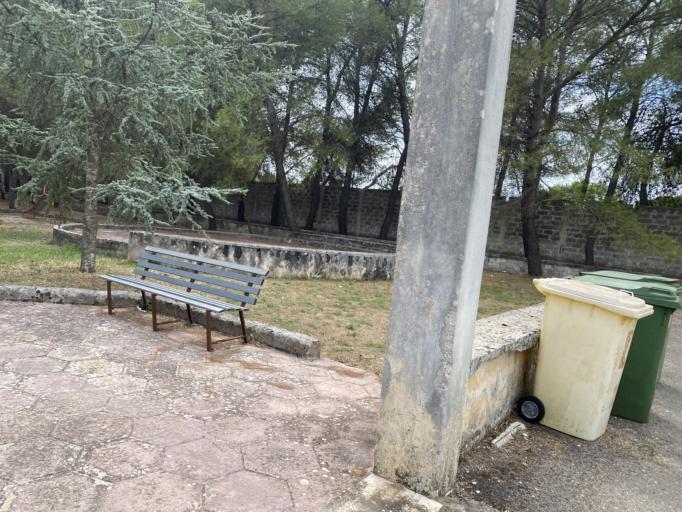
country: IT
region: Apulia
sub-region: Provincia di Lecce
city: Giuggianello
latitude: 40.0868
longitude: 18.3707
